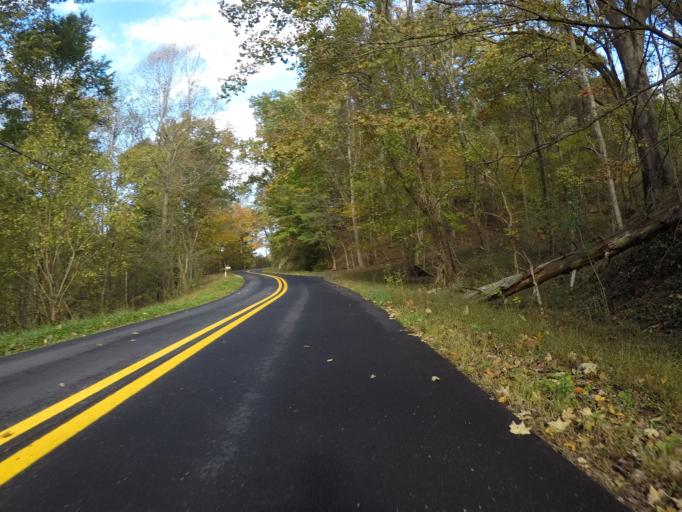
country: US
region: West Virginia
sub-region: Wayne County
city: Lavalette
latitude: 38.3686
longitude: -82.4311
